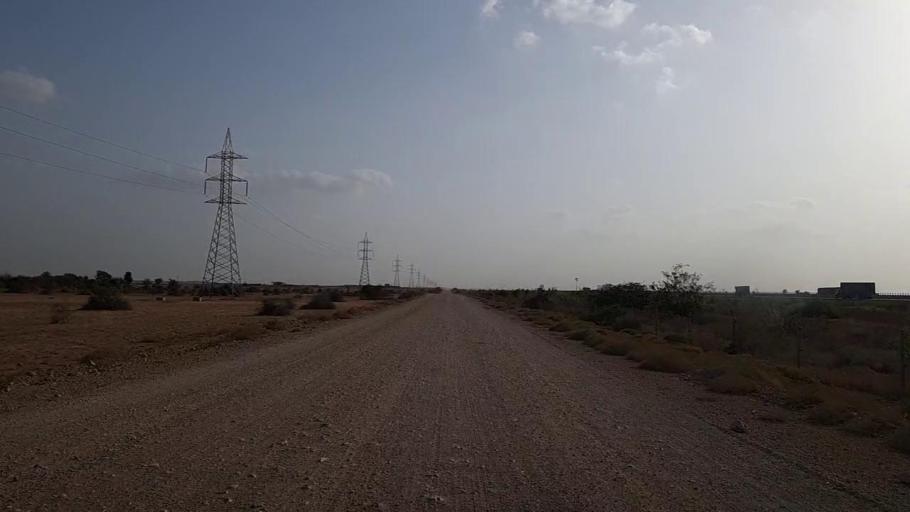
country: PK
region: Sindh
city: Kotri
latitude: 25.2110
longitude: 67.8982
